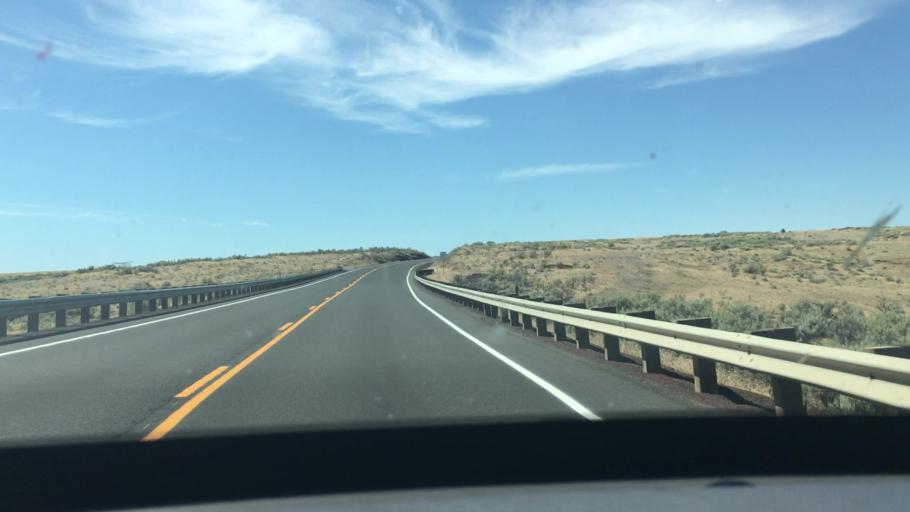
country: US
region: Oregon
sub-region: Sherman County
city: Moro
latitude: 45.2637
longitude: -120.7433
